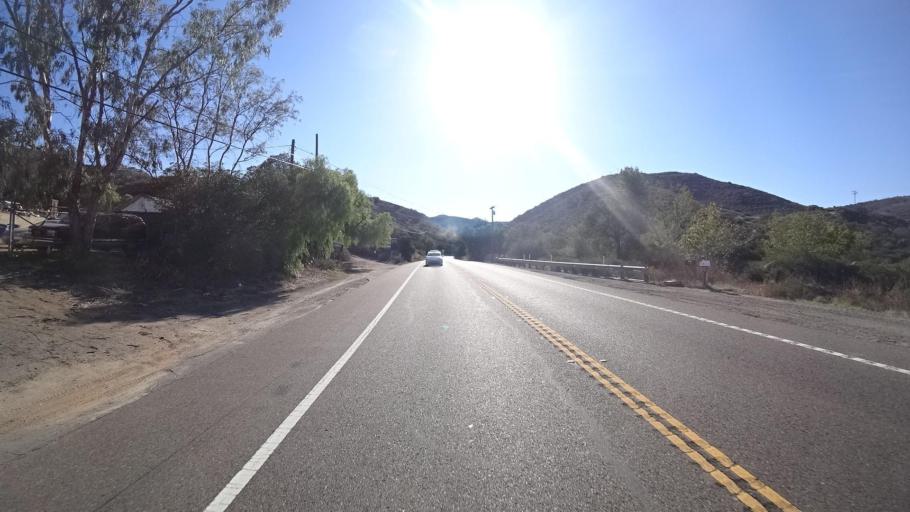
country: US
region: California
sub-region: San Diego County
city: Jamul
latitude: 32.6407
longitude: -116.7721
